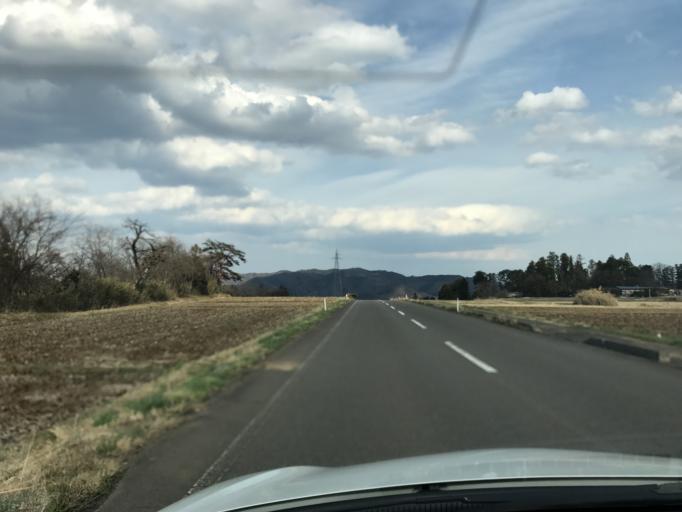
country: JP
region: Miyagi
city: Shiroishi
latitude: 38.0139
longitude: 140.5994
